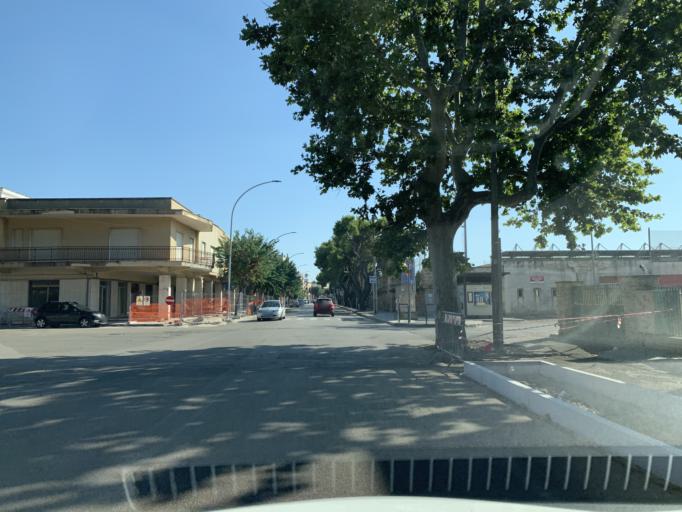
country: IT
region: Apulia
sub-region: Provincia di Lecce
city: Nardo
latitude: 40.1839
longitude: 18.0375
